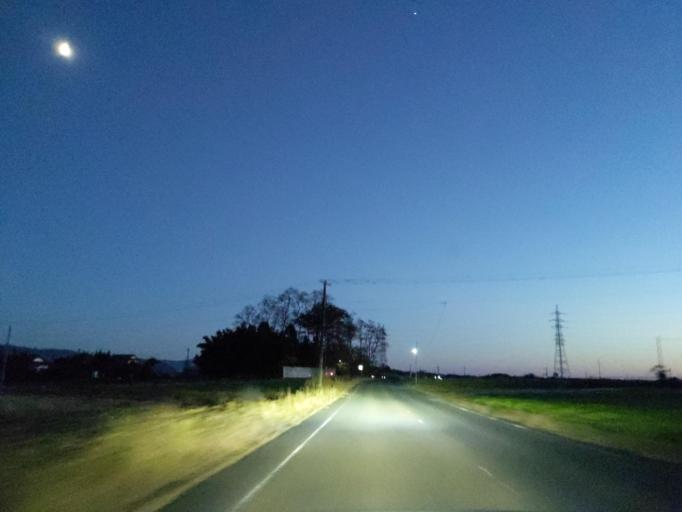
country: JP
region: Fukushima
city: Sukagawa
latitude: 37.3252
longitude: 140.3897
